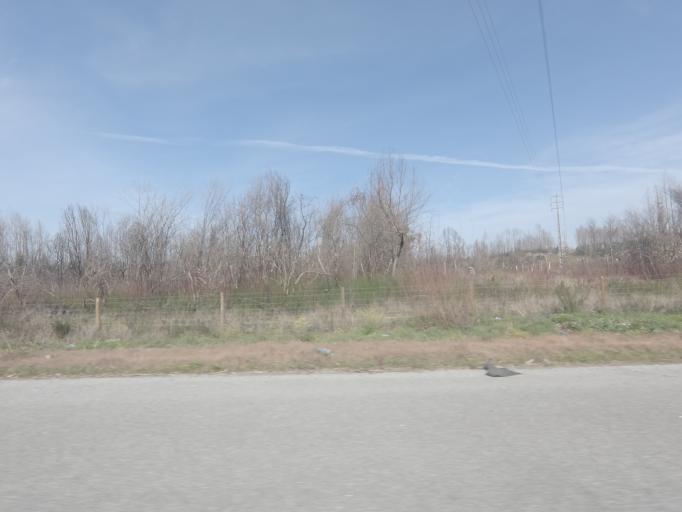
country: PT
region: Viseu
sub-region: Oliveira de Frades
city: Oliveira de Frades
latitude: 40.6855
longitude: -8.2080
